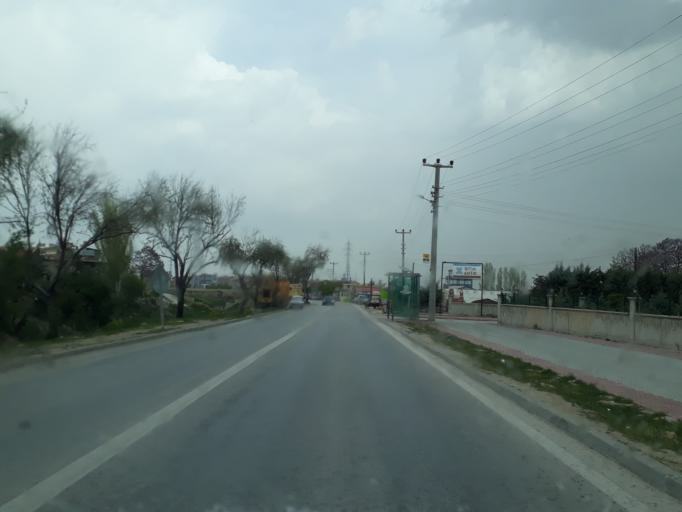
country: TR
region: Konya
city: Selcuklu
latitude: 37.9184
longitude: 32.4656
